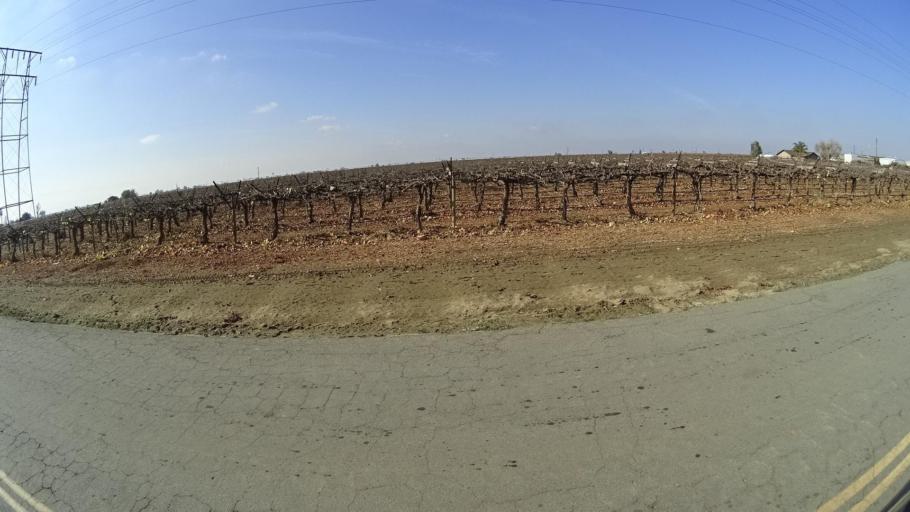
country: US
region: California
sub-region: Kern County
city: Arvin
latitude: 35.2191
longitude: -118.8064
